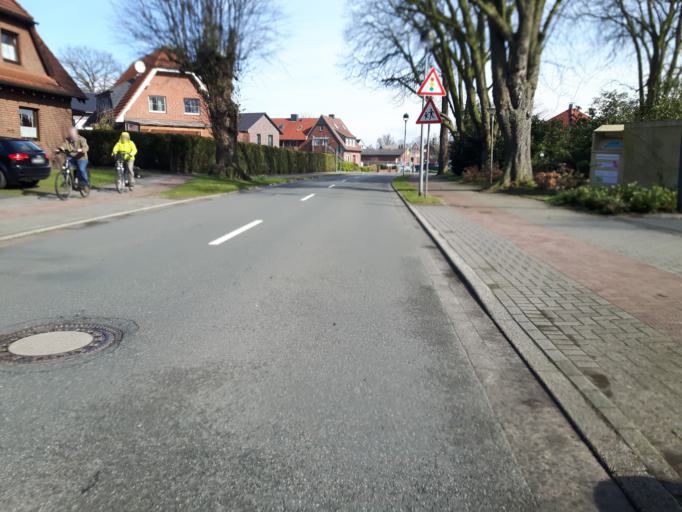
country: DE
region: North Rhine-Westphalia
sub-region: Regierungsbezirk Munster
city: Haltern
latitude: 51.7742
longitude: 7.2228
